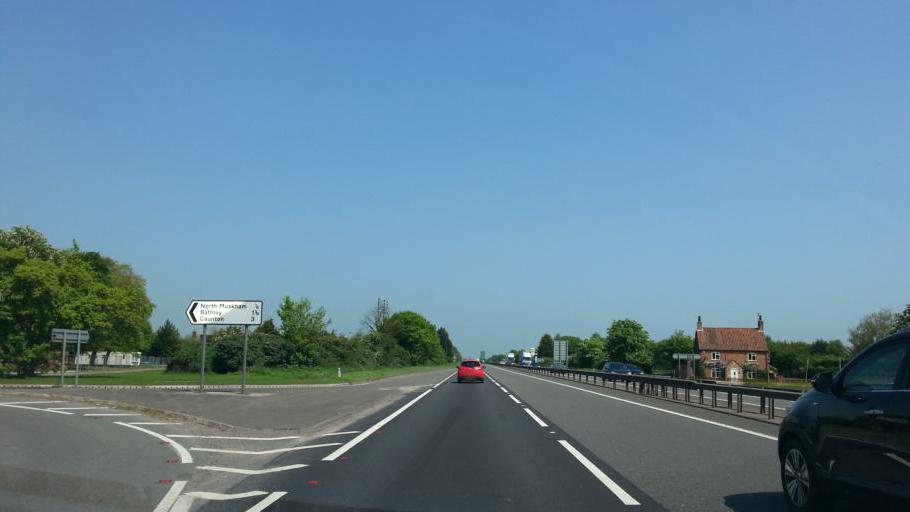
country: GB
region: England
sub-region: Nottinghamshire
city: South Collingham
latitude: 53.1270
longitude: -0.8141
